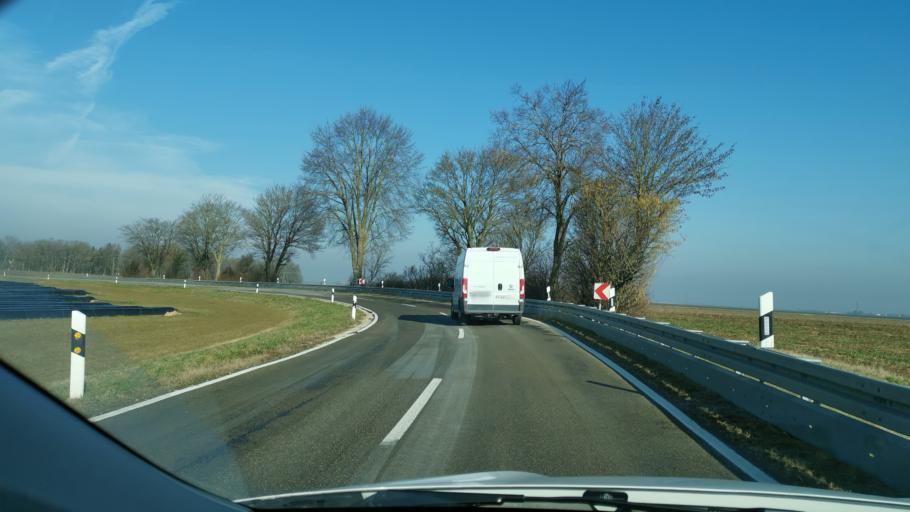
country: DE
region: Bavaria
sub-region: Swabia
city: Munster
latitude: 48.6362
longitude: 10.9258
